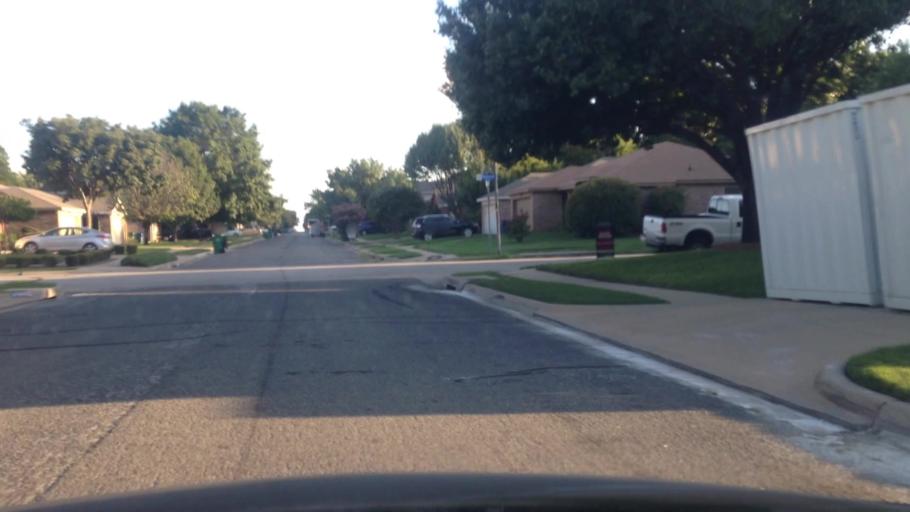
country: US
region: Texas
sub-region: Tarrant County
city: Watauga
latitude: 32.8727
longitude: -97.2490
